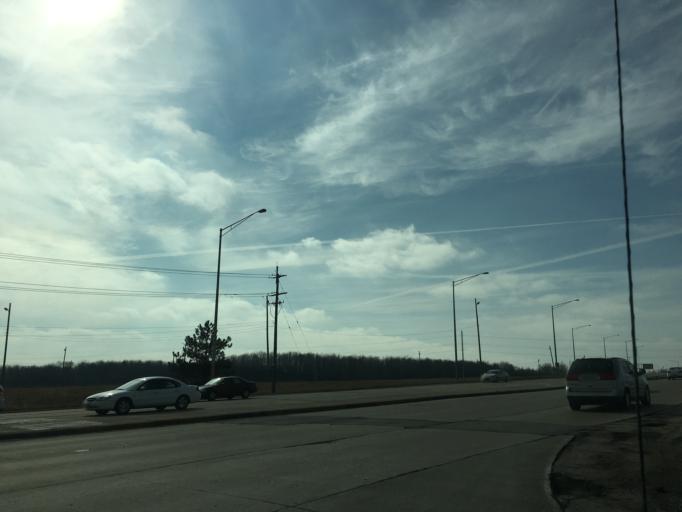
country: US
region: Illinois
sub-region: Cook County
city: Streamwood
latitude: 42.0692
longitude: -88.1917
